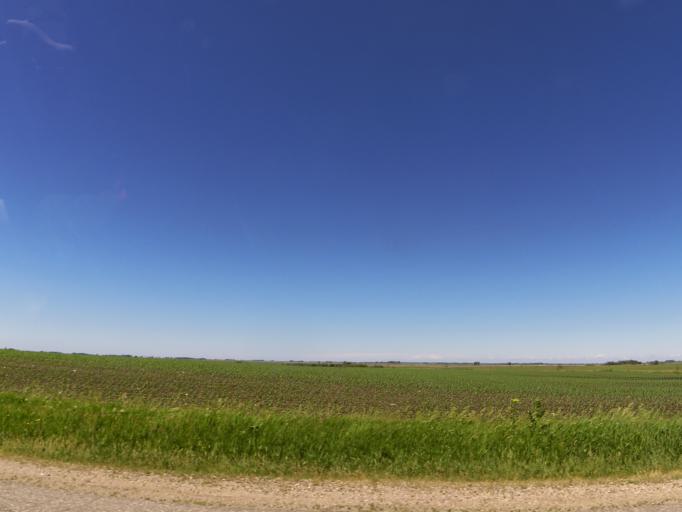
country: US
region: Minnesota
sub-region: Mahnomen County
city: Mahnomen
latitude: 47.1436
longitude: -95.9268
